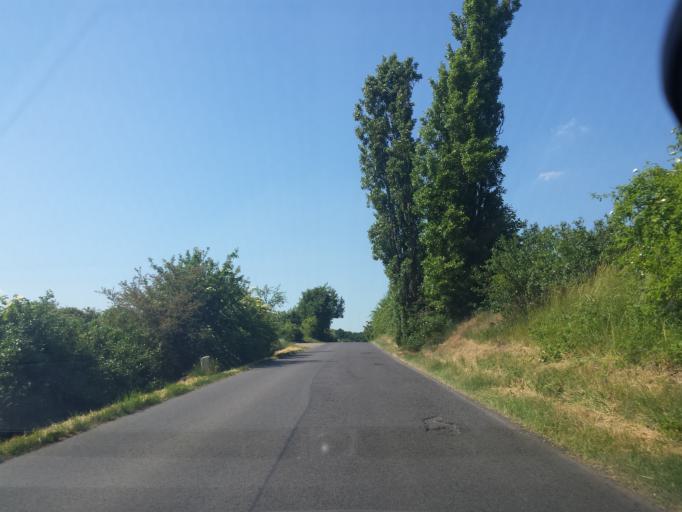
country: CZ
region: Central Bohemia
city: Nelahozeves
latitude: 50.2502
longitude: 14.2987
